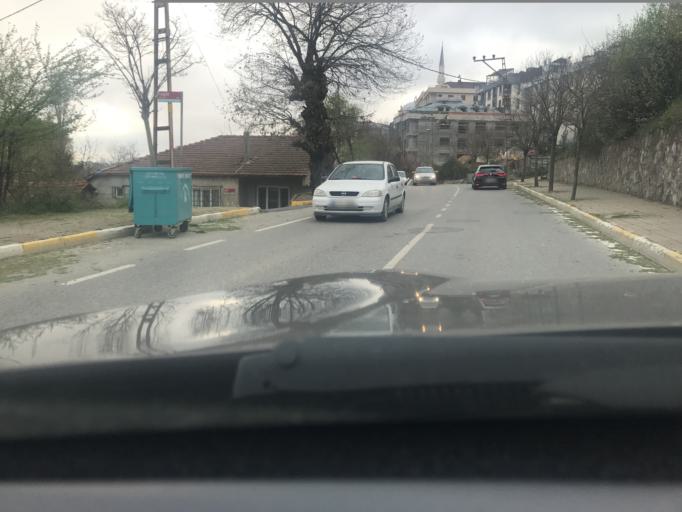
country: TR
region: Istanbul
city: Umraniye
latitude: 41.0362
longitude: 29.1688
